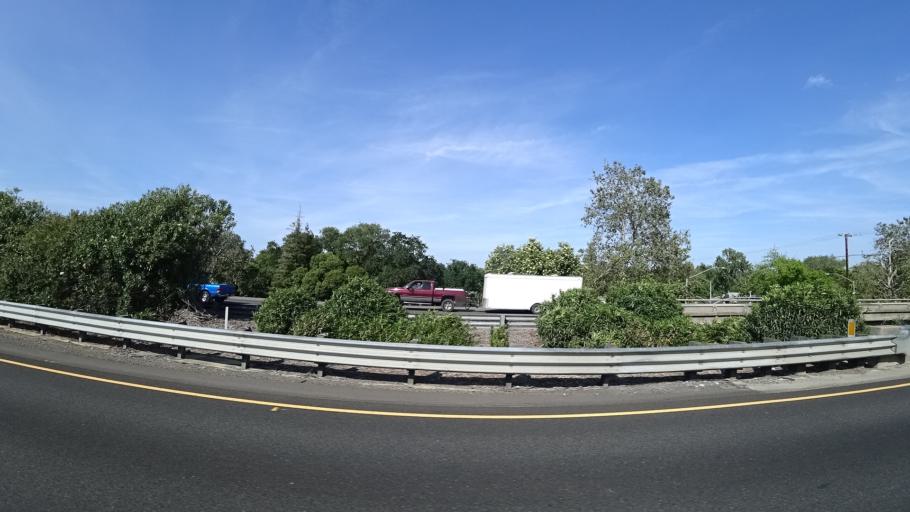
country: US
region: California
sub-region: Butte County
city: Chico
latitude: 39.7456
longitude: -121.8322
